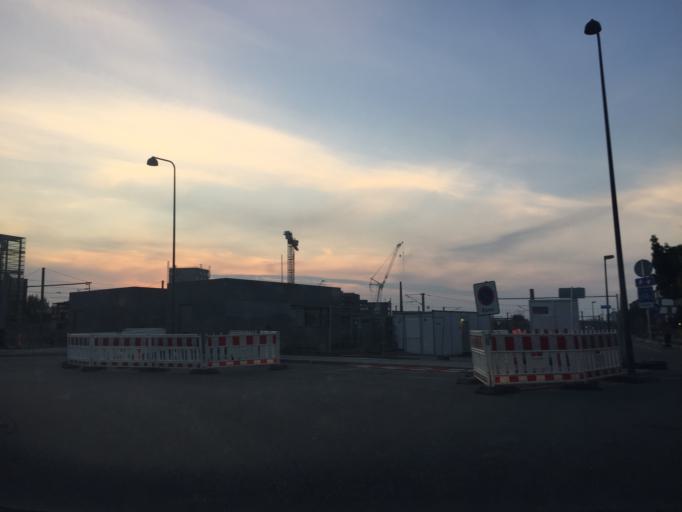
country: DK
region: Capital Region
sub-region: Frederiksberg Kommune
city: Frederiksberg
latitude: 55.6528
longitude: 12.5172
